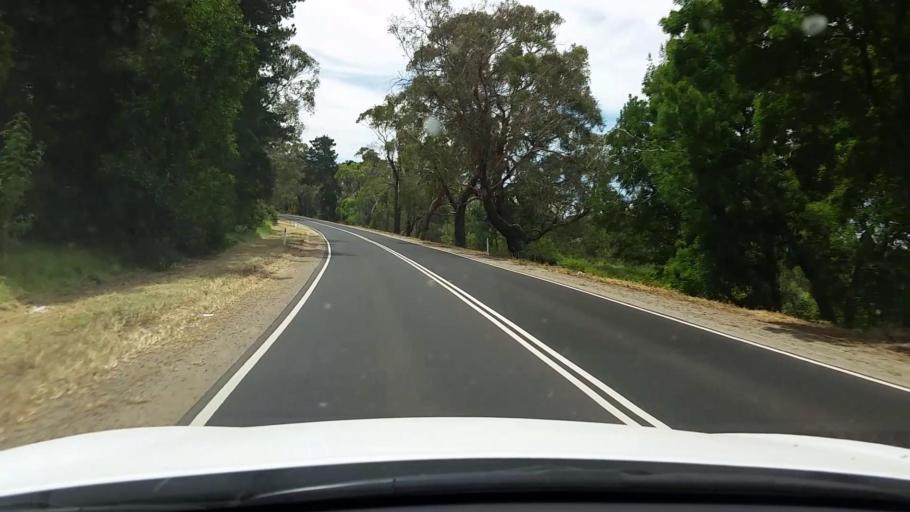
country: AU
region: Victoria
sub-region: Mornington Peninsula
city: Mount Martha
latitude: -38.2786
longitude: 145.0712
